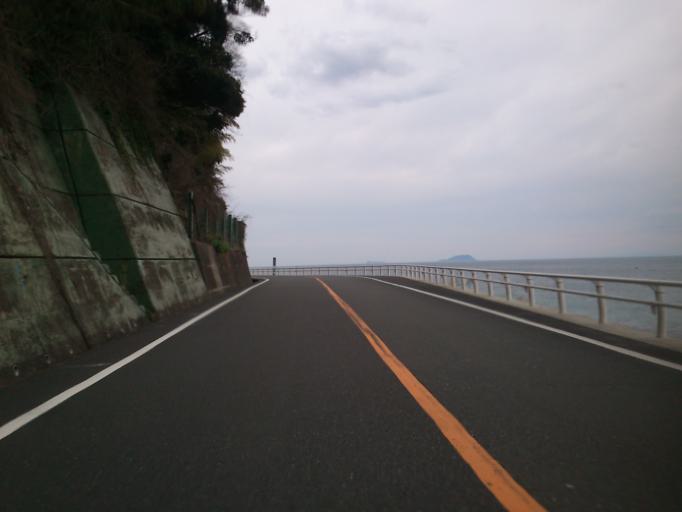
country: JP
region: Kyoto
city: Miyazu
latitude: 35.6202
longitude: 135.2440
